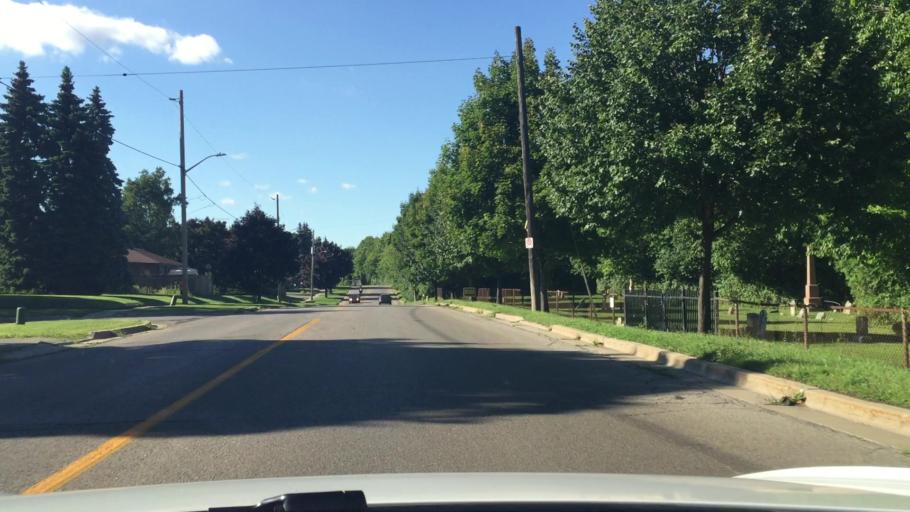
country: CA
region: Ontario
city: Oshawa
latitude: 43.9027
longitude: -78.8768
